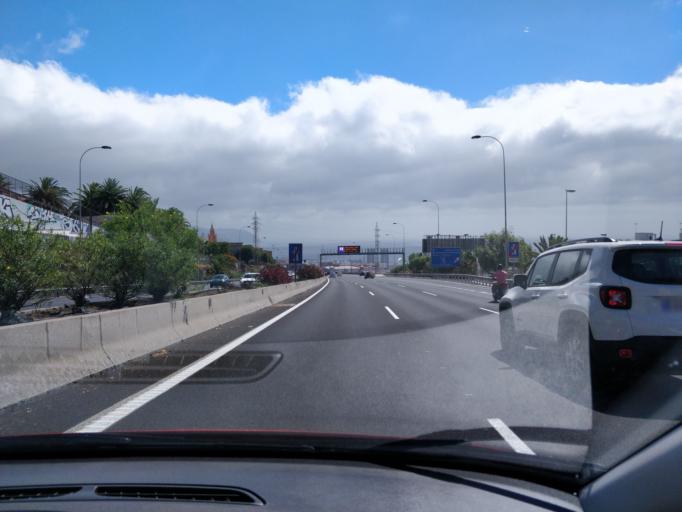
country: ES
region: Canary Islands
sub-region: Provincia de Santa Cruz de Tenerife
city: Santa Cruz de Tenerife
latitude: 28.4477
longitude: -16.2838
